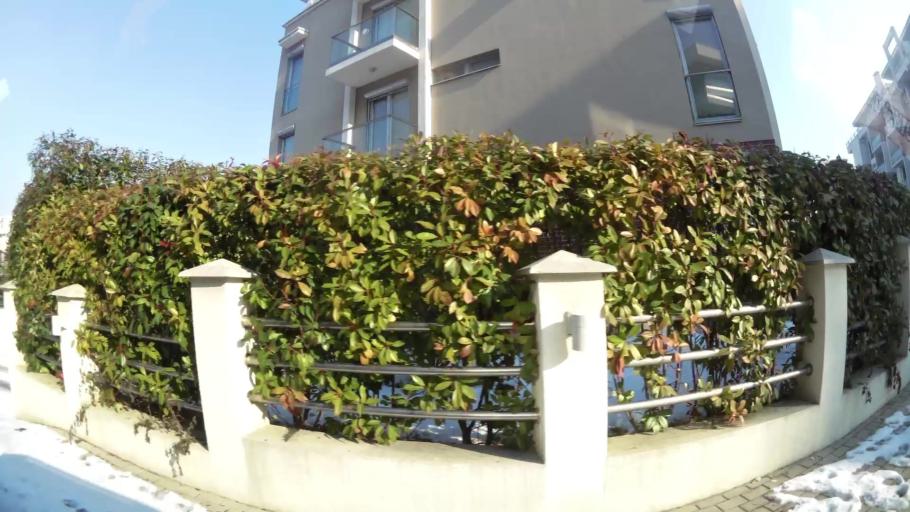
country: MK
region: Karpos
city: Skopje
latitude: 41.9814
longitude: 21.4233
